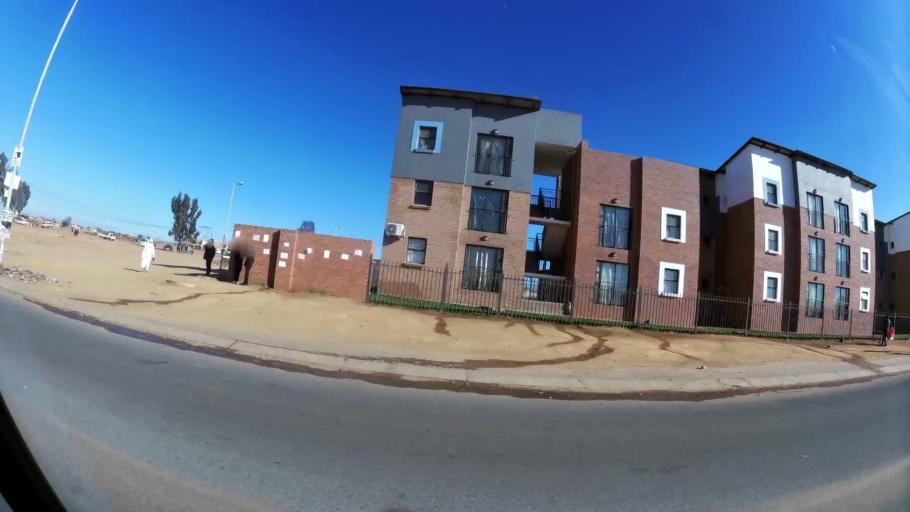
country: ZA
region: Gauteng
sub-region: City of Johannesburg Metropolitan Municipality
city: Diepsloot
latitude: -25.9035
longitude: 28.0962
